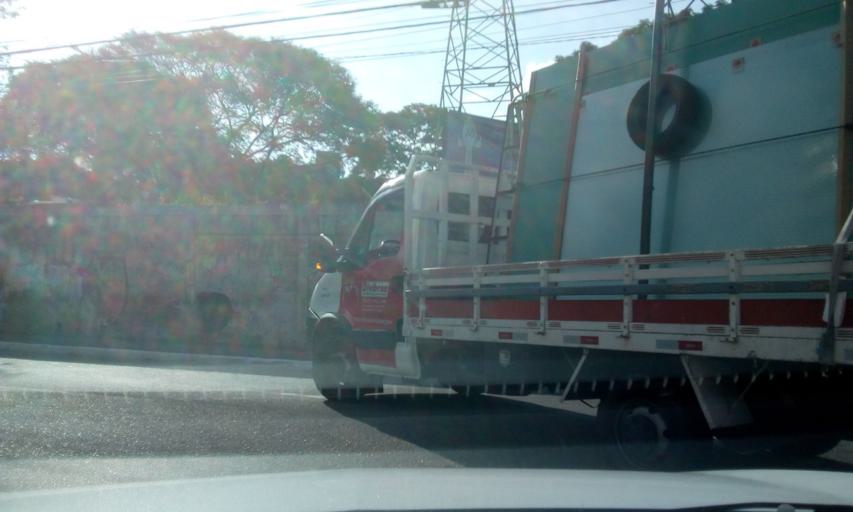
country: BR
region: Sao Paulo
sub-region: Sao Paulo
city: Sao Paulo
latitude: -23.5039
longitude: -46.6800
